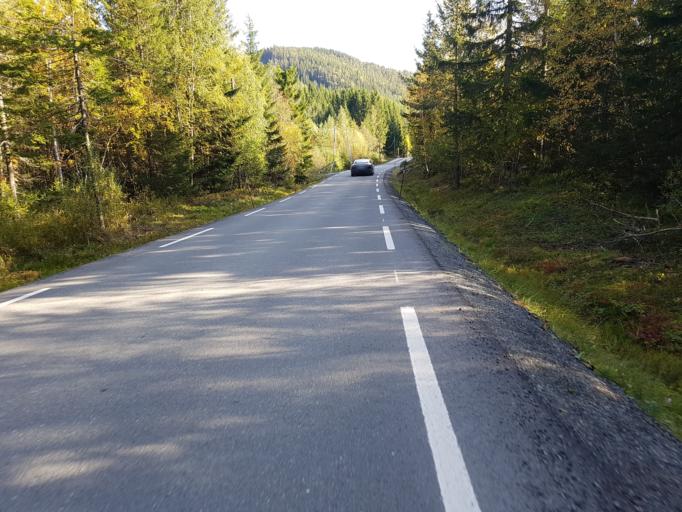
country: NO
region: Sor-Trondelag
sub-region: Malvik
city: Malvik
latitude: 63.3775
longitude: 10.6027
